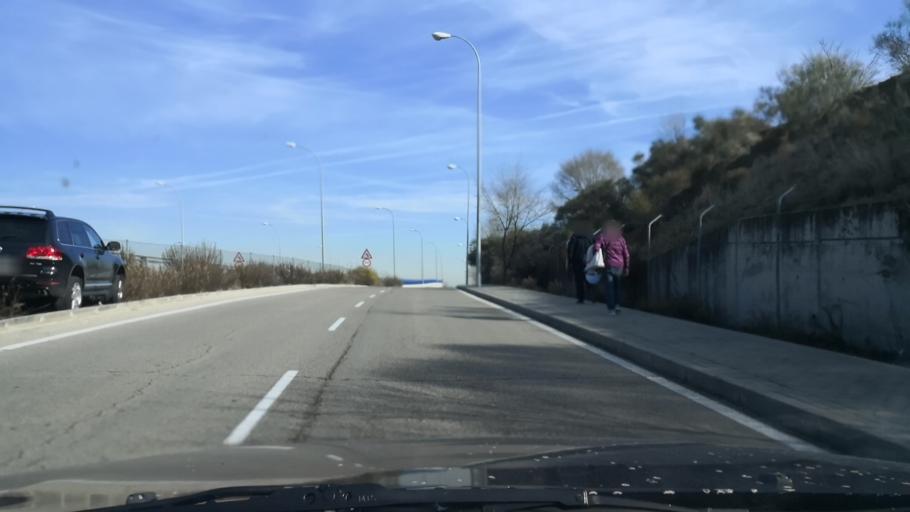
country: ES
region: Madrid
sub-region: Provincia de Madrid
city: Hortaleza
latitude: 40.4719
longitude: -3.6228
